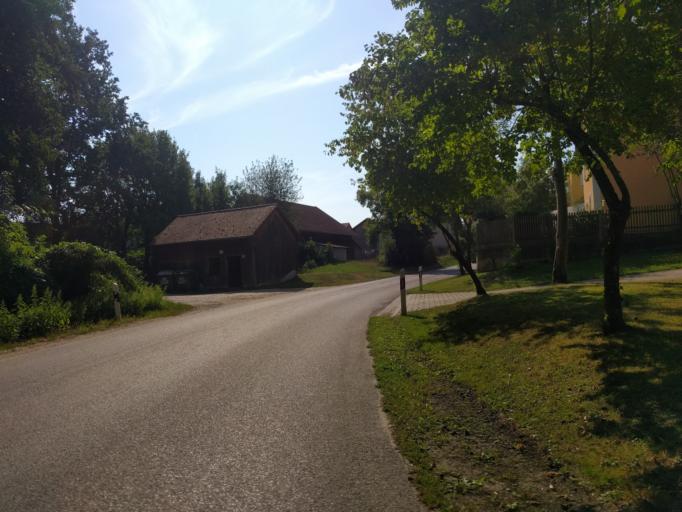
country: DE
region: Bavaria
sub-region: Upper Palatinate
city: Donaustauf
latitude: 49.0169
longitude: 12.2311
